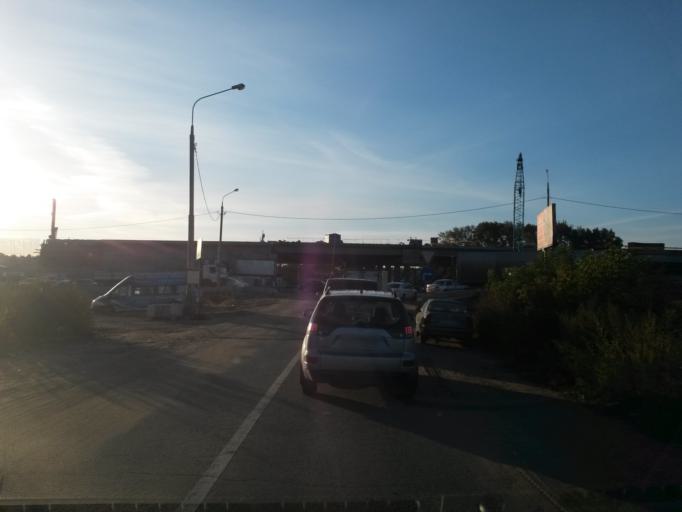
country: RU
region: Moskovskaya
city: Mamontovka
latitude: 55.9654
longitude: 37.8378
